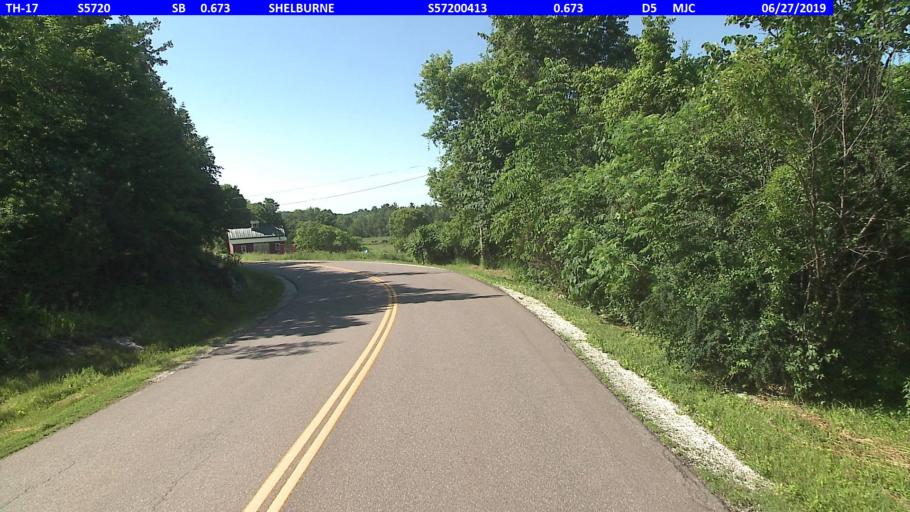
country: US
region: Vermont
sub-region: Chittenden County
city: Hinesburg
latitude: 44.3674
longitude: -73.2015
